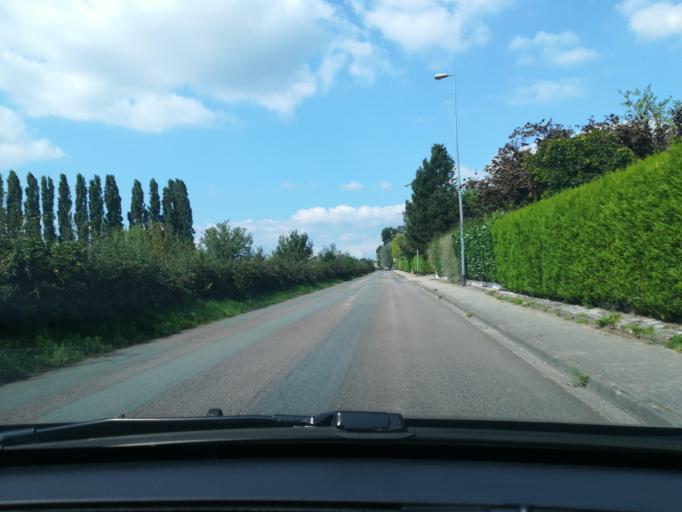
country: FR
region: Haute-Normandie
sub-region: Departement de la Seine-Maritime
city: Bois-Guillaume
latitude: 49.4630
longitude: 1.1088
